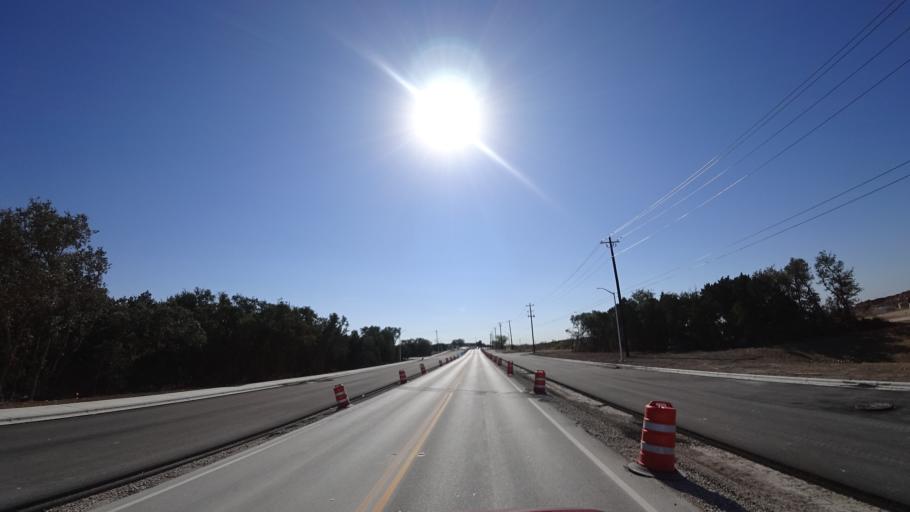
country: US
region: Texas
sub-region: Williamson County
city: Cedar Park
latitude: 30.5112
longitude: -97.8577
